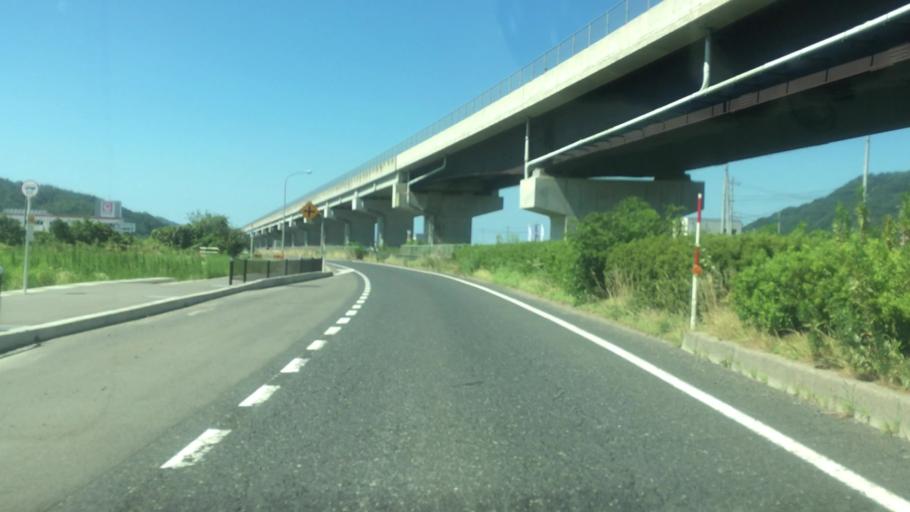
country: JP
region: Tottori
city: Tottori
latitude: 35.4257
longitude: 134.2071
